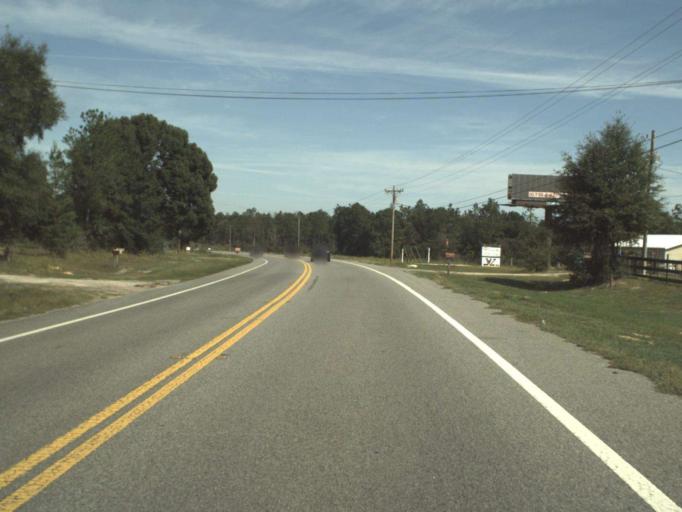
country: US
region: Florida
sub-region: Bay County
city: Lynn Haven
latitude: 30.4741
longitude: -85.6657
